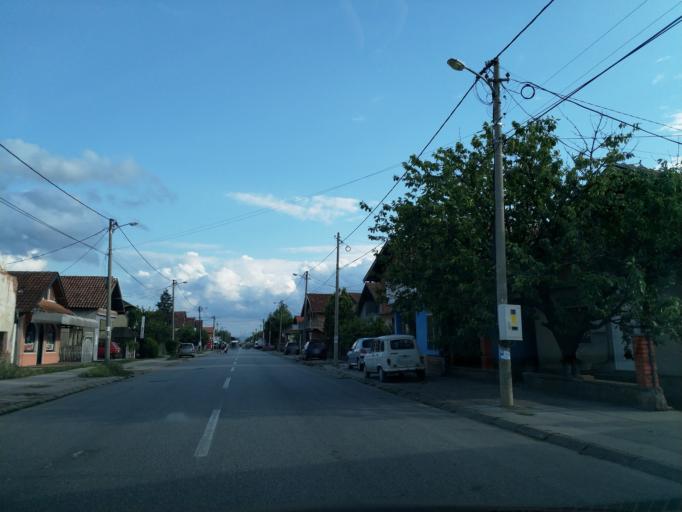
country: RS
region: Central Serbia
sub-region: Pomoravski Okrug
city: Paracin
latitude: 43.8497
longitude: 21.4136
